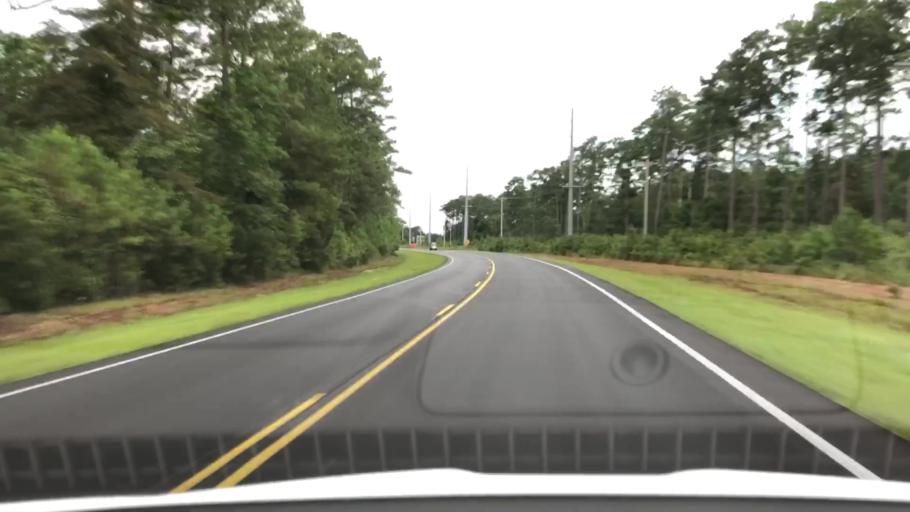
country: US
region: North Carolina
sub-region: Onslow County
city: Swansboro
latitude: 34.7859
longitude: -77.1177
